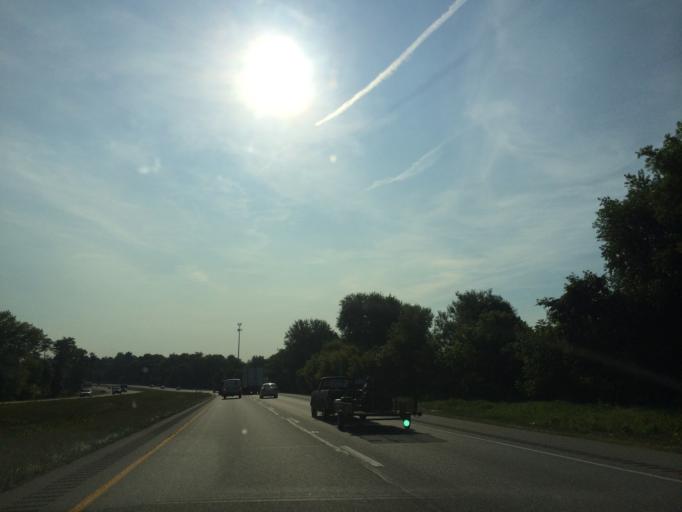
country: US
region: Pennsylvania
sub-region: York County
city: Hallam
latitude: 40.0070
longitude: -76.6089
